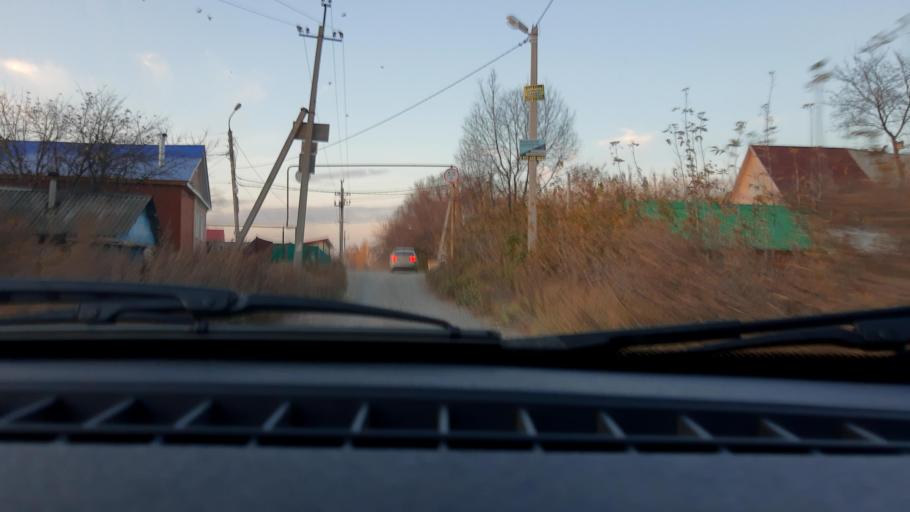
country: RU
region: Bashkortostan
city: Mikhaylovka
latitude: 54.7606
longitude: 55.9137
